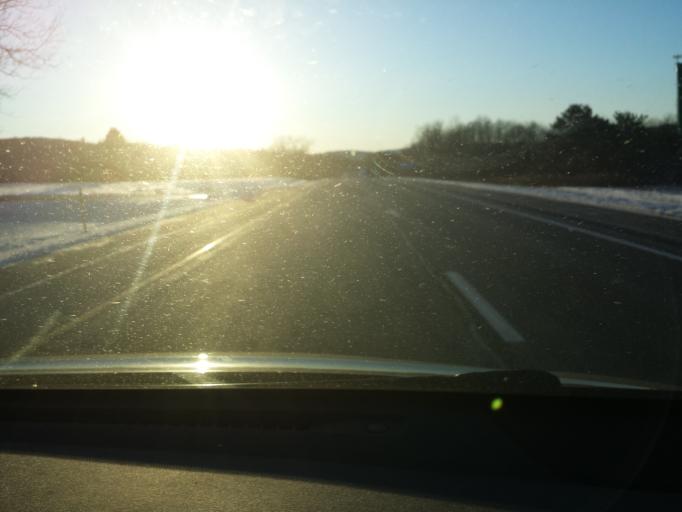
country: US
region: Pennsylvania
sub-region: Clinton County
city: Avis
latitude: 41.0572
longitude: -77.2685
